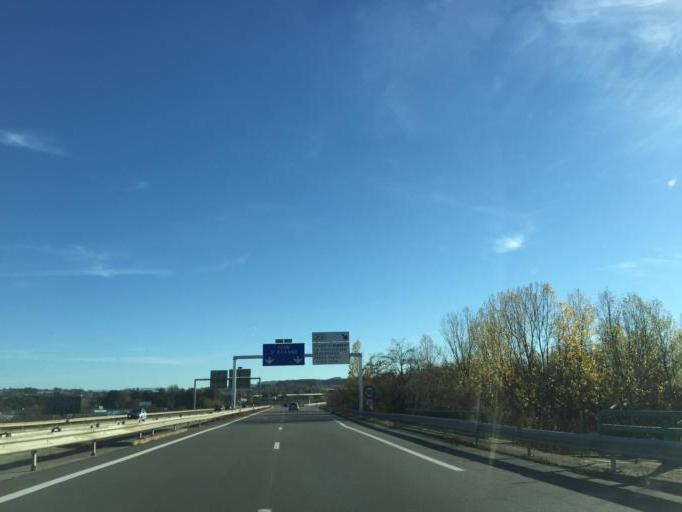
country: FR
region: Rhone-Alpes
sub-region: Departement de la Loire
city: Andrezieux-Boutheon
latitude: 45.5298
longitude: 4.2852
